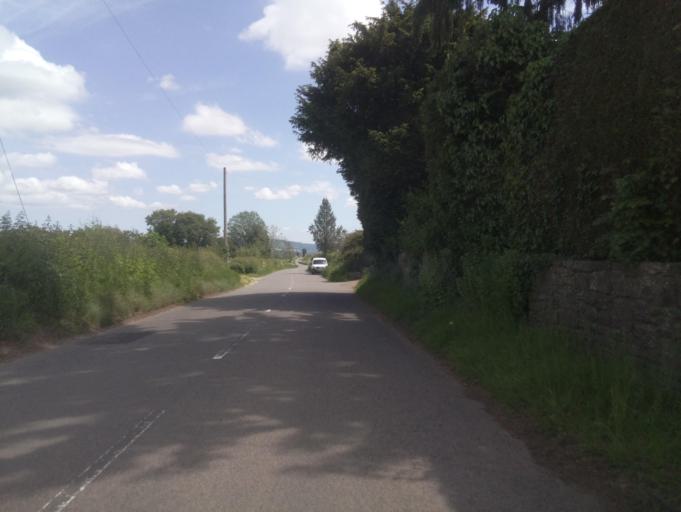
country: GB
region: England
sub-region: Herefordshire
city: Llanrothal
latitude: 51.8498
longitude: -2.7982
